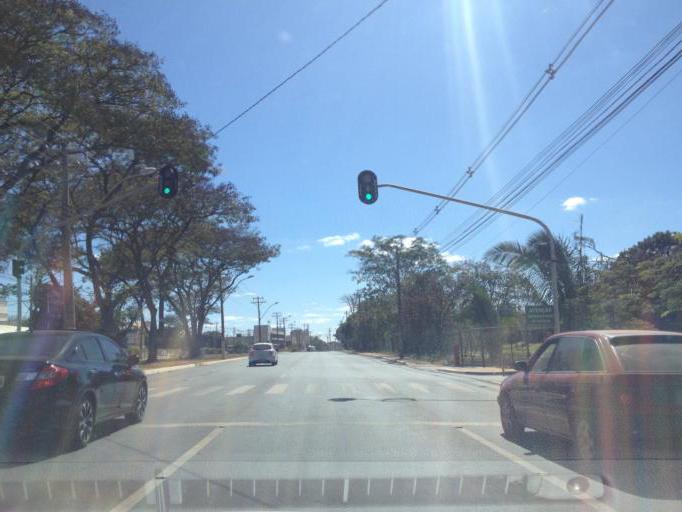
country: BR
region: Federal District
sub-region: Brasilia
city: Brasilia
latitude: -15.8032
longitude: -47.9507
